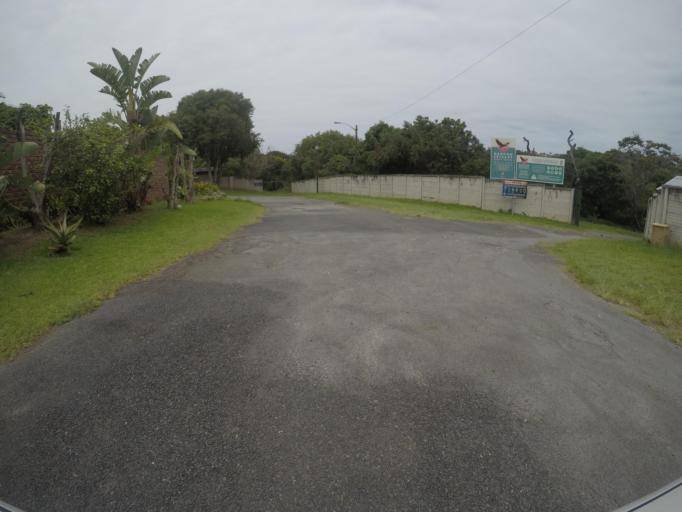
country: ZA
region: Eastern Cape
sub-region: Buffalo City Metropolitan Municipality
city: East London
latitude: -32.9823
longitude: 27.9376
